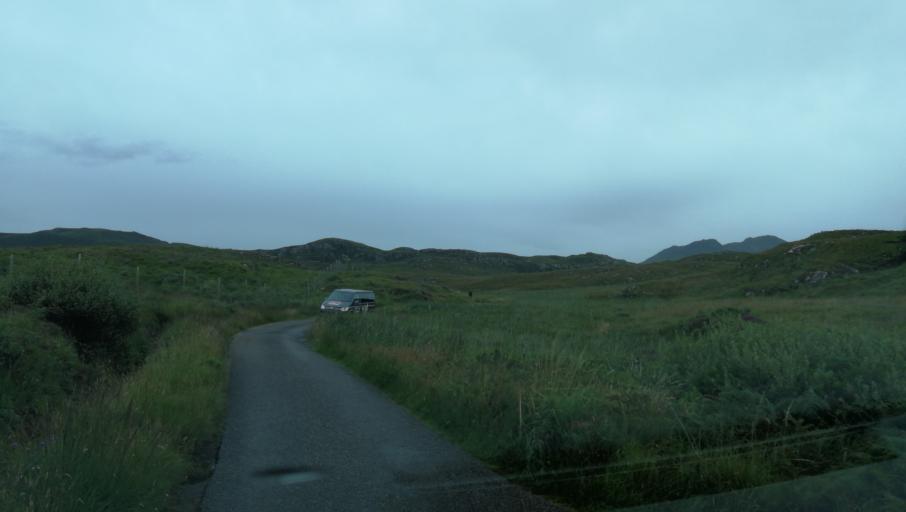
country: GB
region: Scotland
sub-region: Argyll and Bute
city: Isle Of Mull
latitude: 56.7222
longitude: -6.2172
